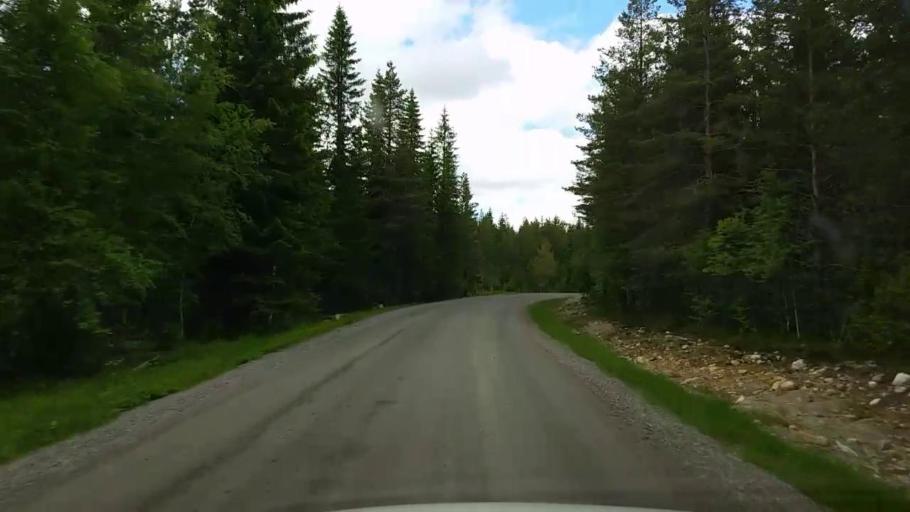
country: SE
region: Gaevleborg
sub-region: Bollnas Kommun
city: Vittsjo
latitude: 61.1614
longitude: 16.1572
